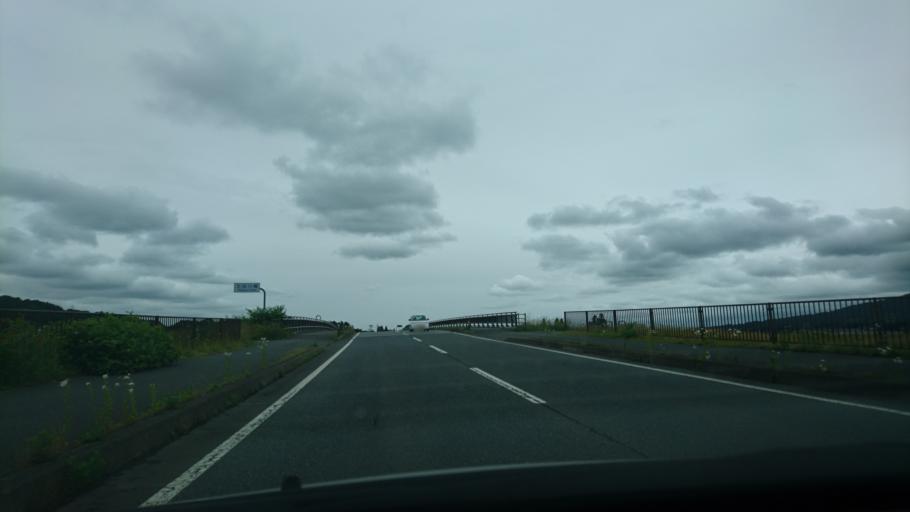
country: JP
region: Iwate
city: Ichinoseki
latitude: 38.9839
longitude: 141.1164
